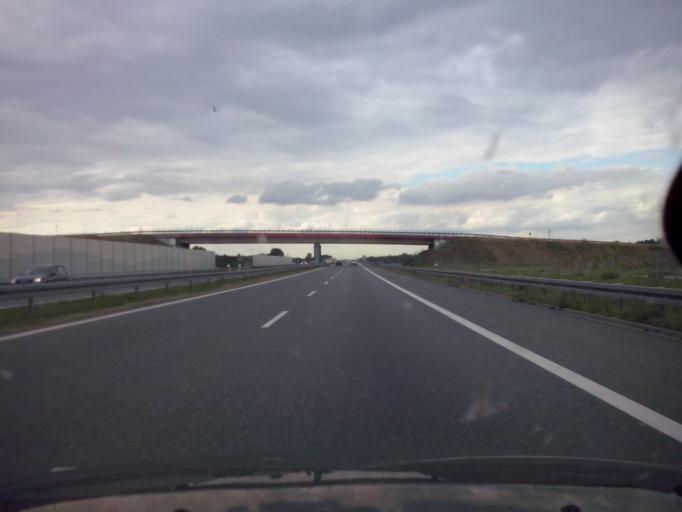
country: PL
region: Lesser Poland Voivodeship
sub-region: Powiat wielicki
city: Podleze
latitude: 50.0077
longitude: 20.1651
